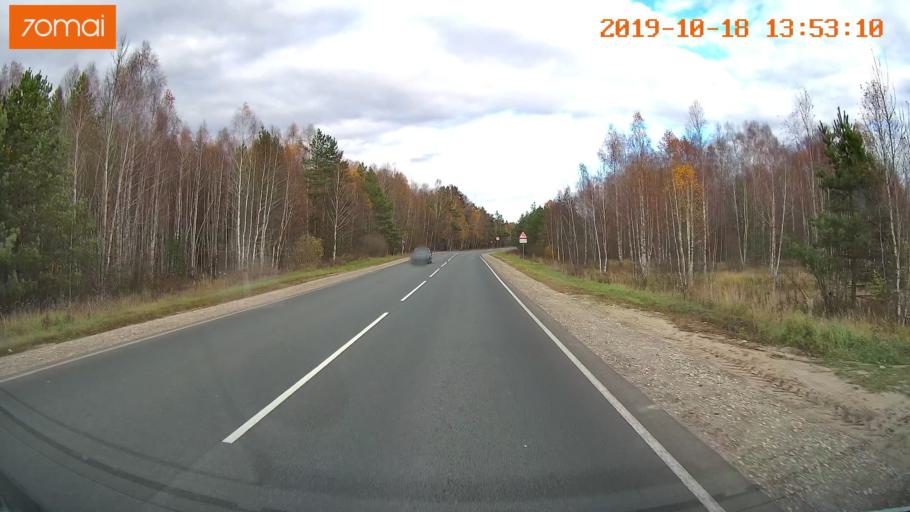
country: RU
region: Moskovskaya
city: Radovitskiy
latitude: 55.0361
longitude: 39.9763
